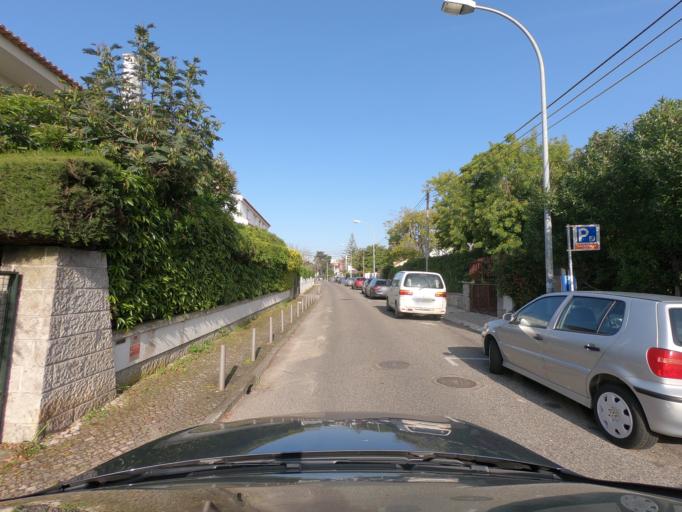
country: PT
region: Lisbon
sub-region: Oeiras
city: Oeiras
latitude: 38.6901
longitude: -9.3165
